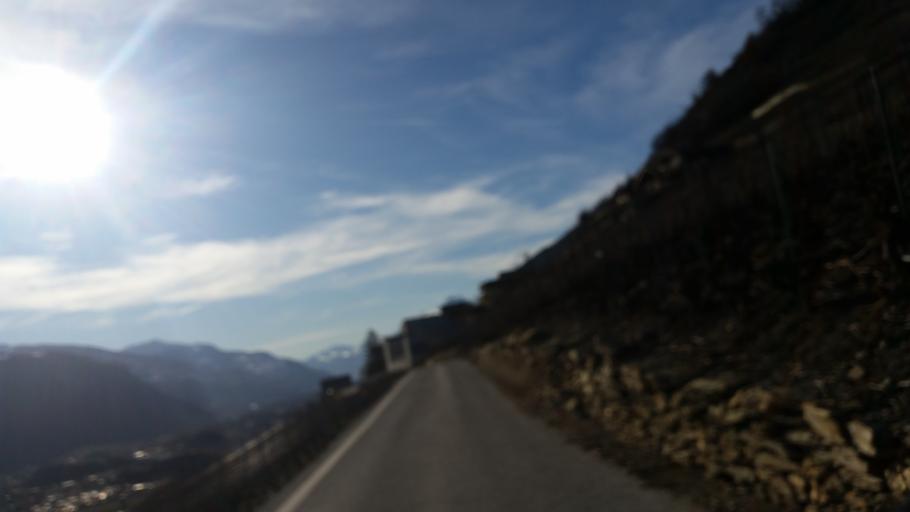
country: CH
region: Valais
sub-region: Sierre District
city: Chermignon-d'en Haut
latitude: 46.2761
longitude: 7.4880
